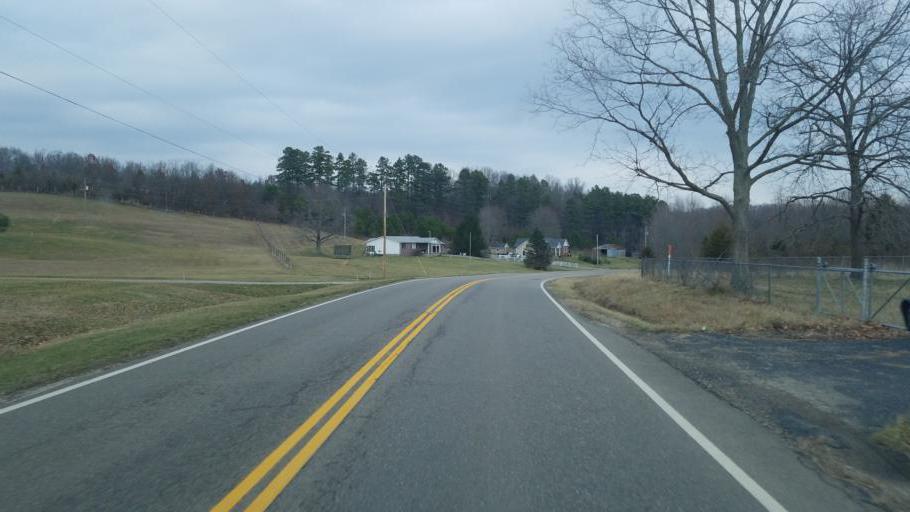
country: US
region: Ohio
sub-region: Gallia County
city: Gallipolis
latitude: 38.8655
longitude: -82.3834
